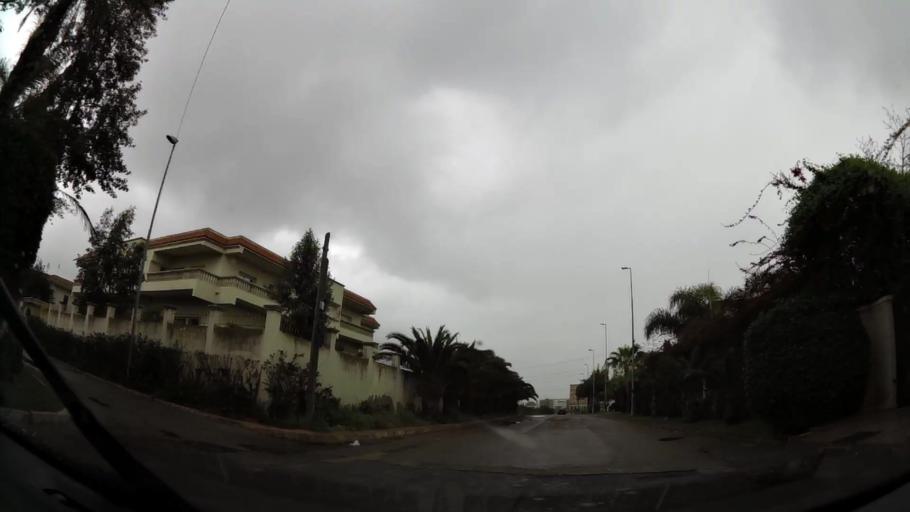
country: MA
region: Grand Casablanca
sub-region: Casablanca
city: Casablanca
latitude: 33.5332
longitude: -7.6199
